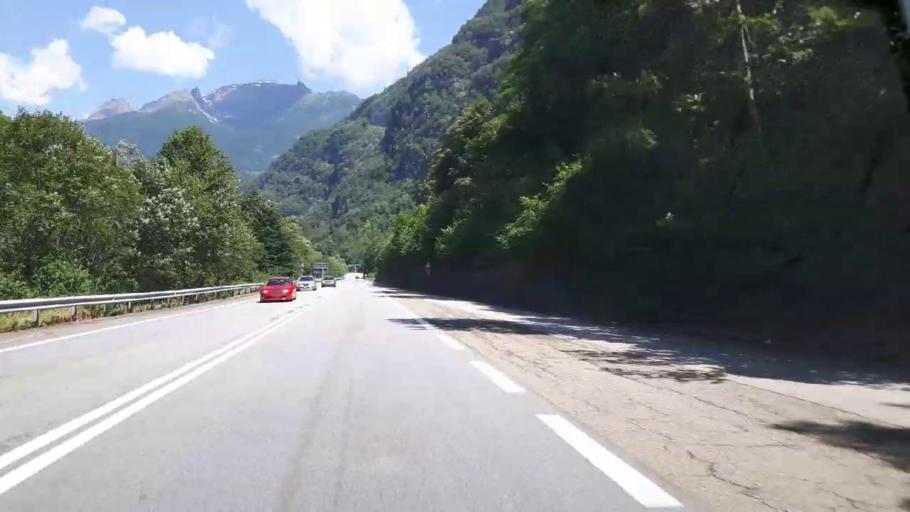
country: IT
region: Piedmont
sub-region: Provincia Verbano-Cusio-Ossola
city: Crevoladossola
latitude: 46.1798
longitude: 8.2804
